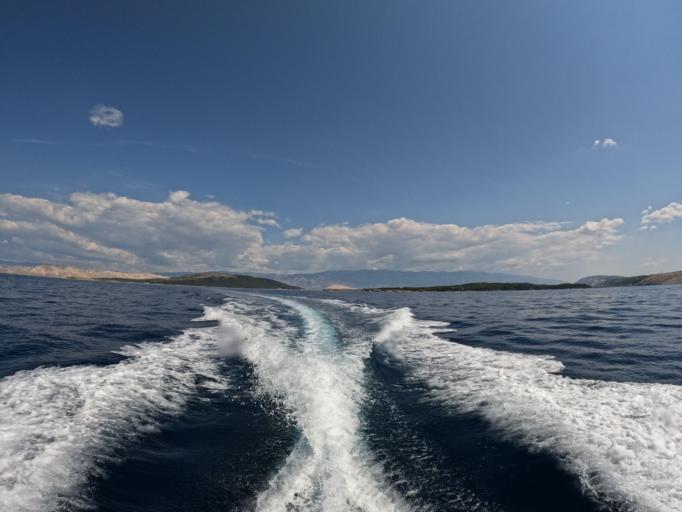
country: HR
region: Primorsko-Goranska
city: Lopar
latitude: 44.8551
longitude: 14.7034
